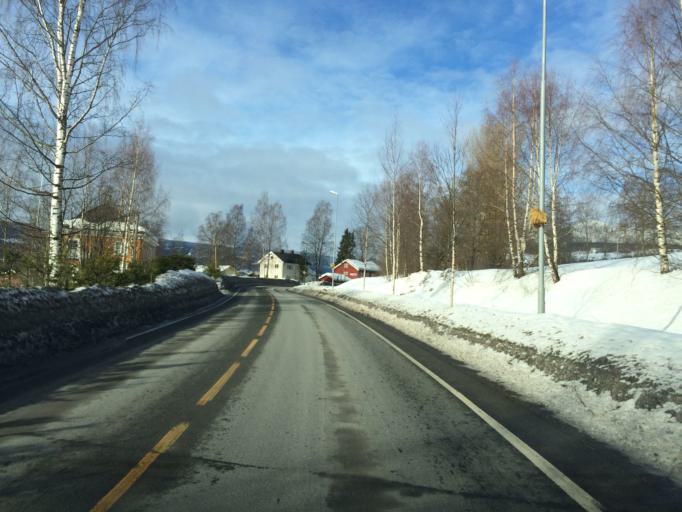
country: NO
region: Oppland
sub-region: Gausdal
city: Segalstad bru
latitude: 61.2143
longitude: 10.2887
